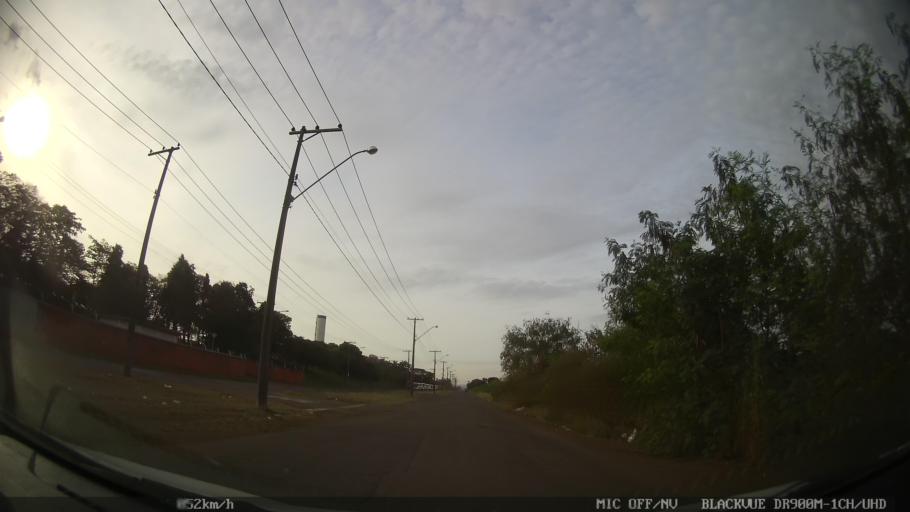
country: BR
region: Sao Paulo
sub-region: Piracicaba
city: Piracicaba
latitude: -22.7298
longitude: -47.5868
